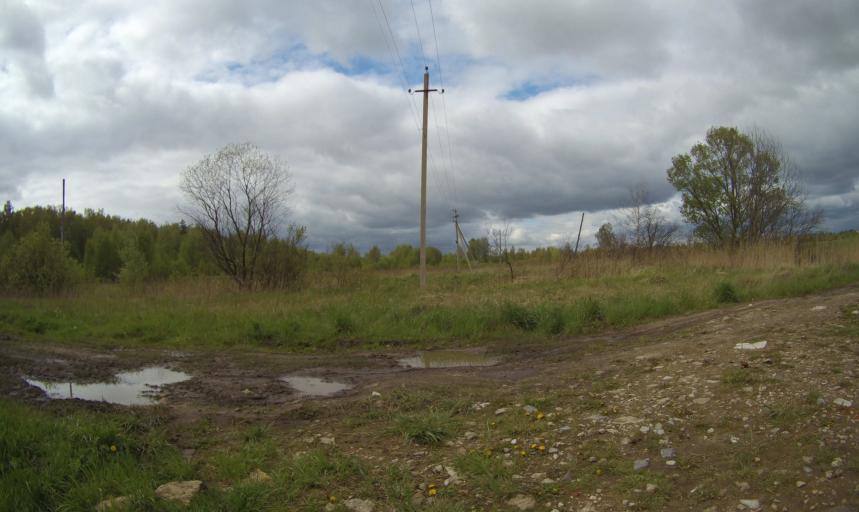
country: RU
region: Moskovskaya
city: Rechitsy
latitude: 55.5692
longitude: 38.4797
